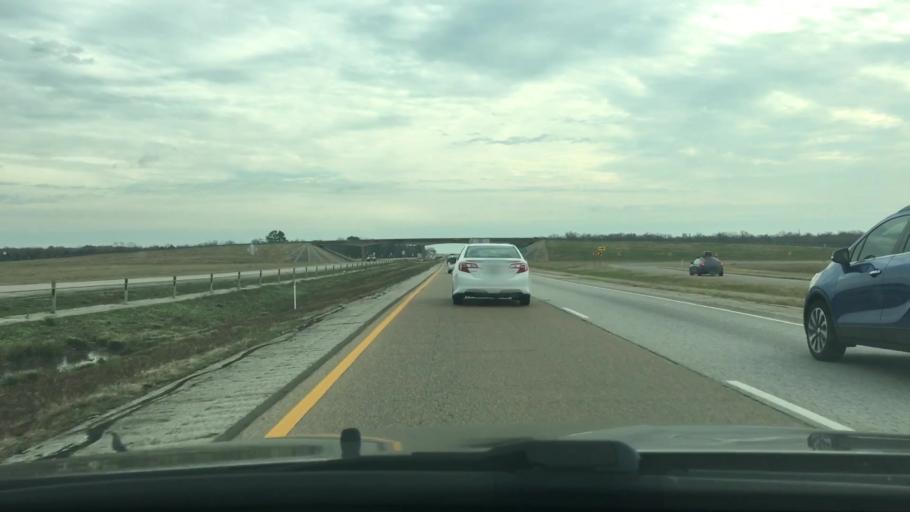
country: US
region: Texas
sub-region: Madison County
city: Madisonville
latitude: 31.0948
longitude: -95.9619
